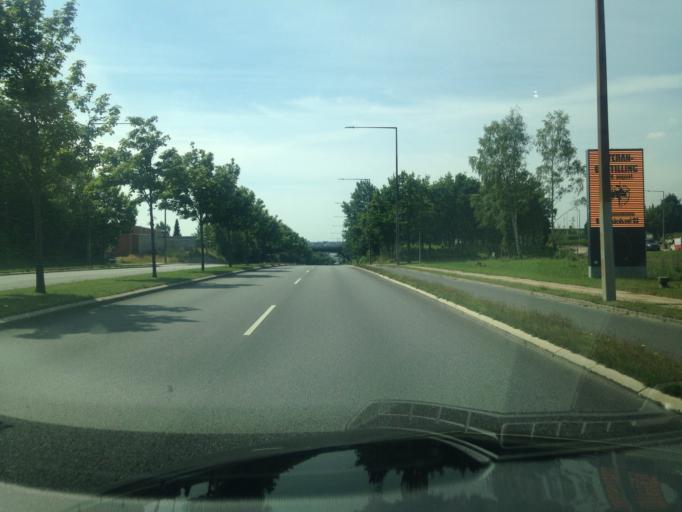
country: DK
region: South Denmark
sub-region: Kolding Kommune
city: Kolding
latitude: 55.5030
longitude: 9.5026
